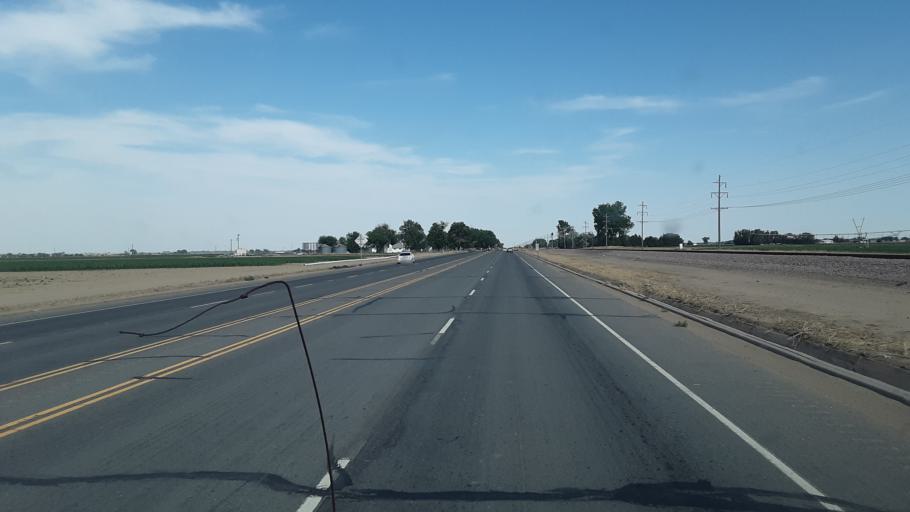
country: US
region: Colorado
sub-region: Otero County
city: Rocky Ford
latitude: 38.0787
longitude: -103.7836
